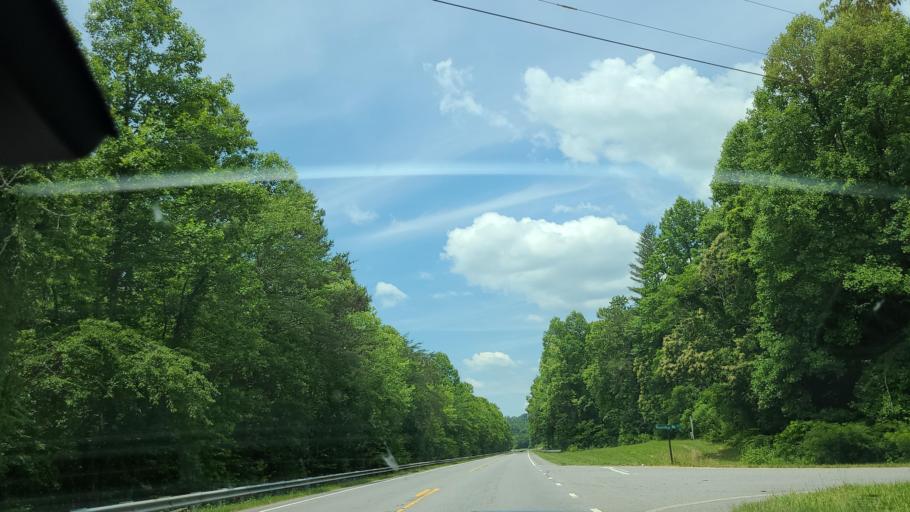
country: US
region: Georgia
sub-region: Towns County
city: Hiawassee
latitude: 35.0231
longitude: -83.6982
